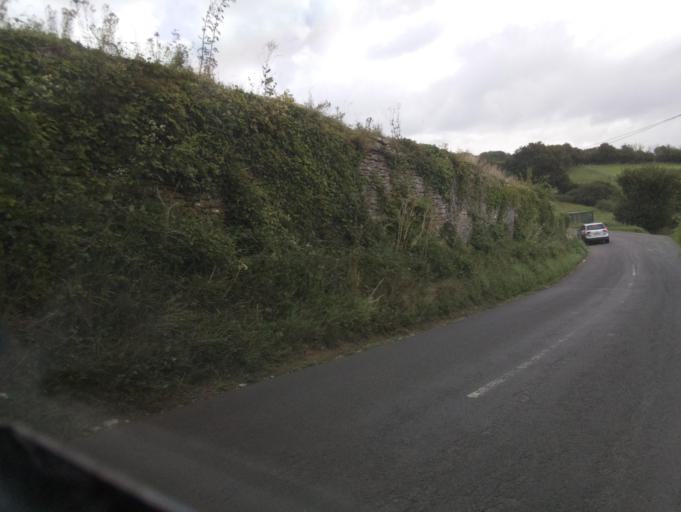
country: GB
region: England
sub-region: Dorset
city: Stalbridge
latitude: 50.9538
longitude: -2.3909
